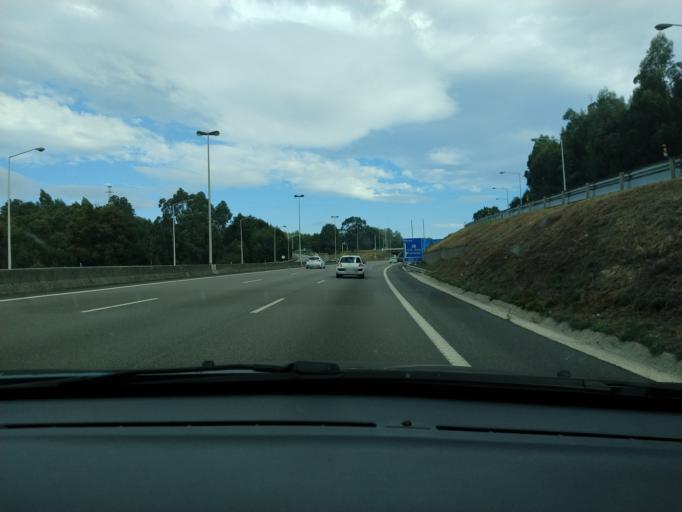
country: PT
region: Porto
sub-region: Vila Nova de Gaia
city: Perozinho
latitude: 41.0691
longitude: -8.5819
